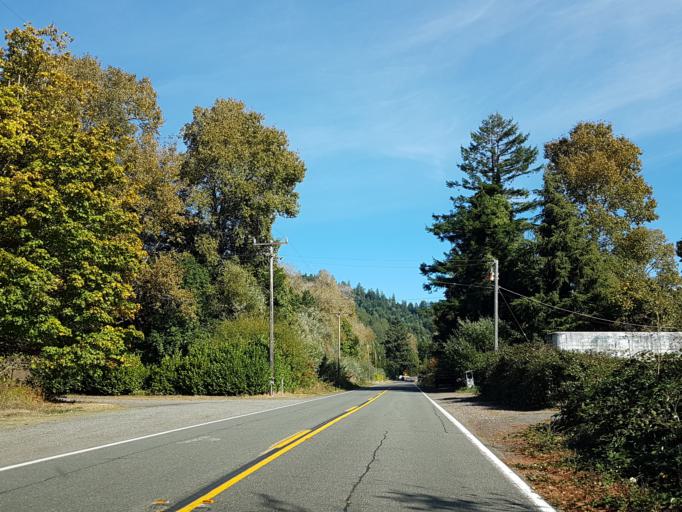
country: US
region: California
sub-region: Humboldt County
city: Rio Dell
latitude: 40.4461
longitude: -123.9936
